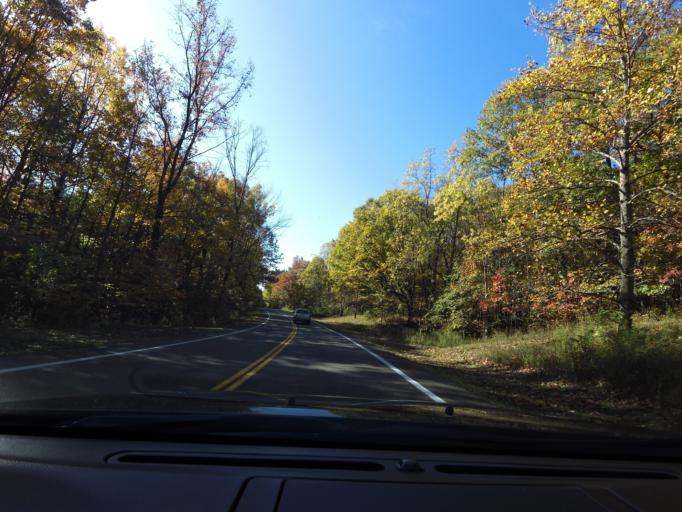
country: US
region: New York
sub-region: Wyoming County
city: Castile
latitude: 42.6410
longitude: -77.9882
